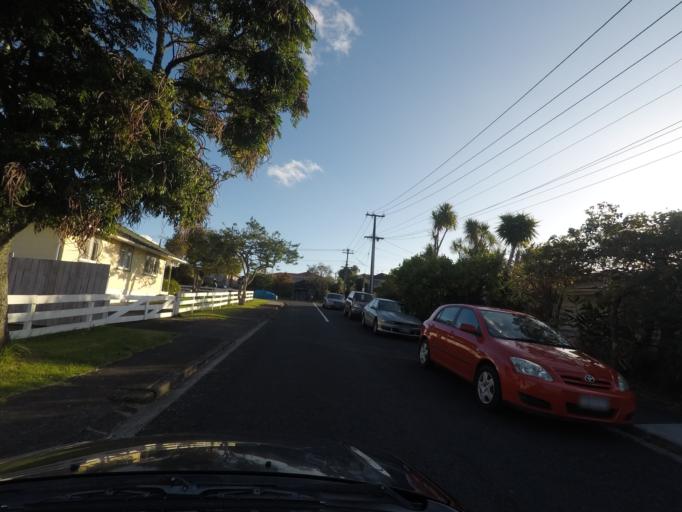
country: NZ
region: Auckland
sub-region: Auckland
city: Waitakere
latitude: -36.9036
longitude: 174.6769
